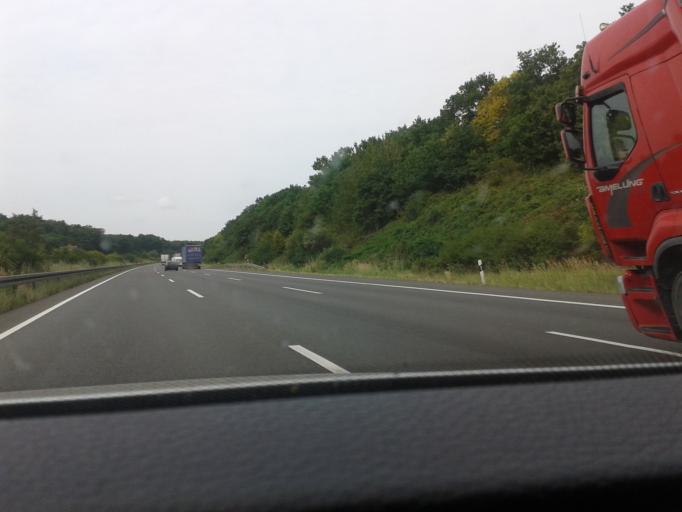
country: DE
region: Lower Saxony
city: Rennau
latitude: 52.2828
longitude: 10.9113
